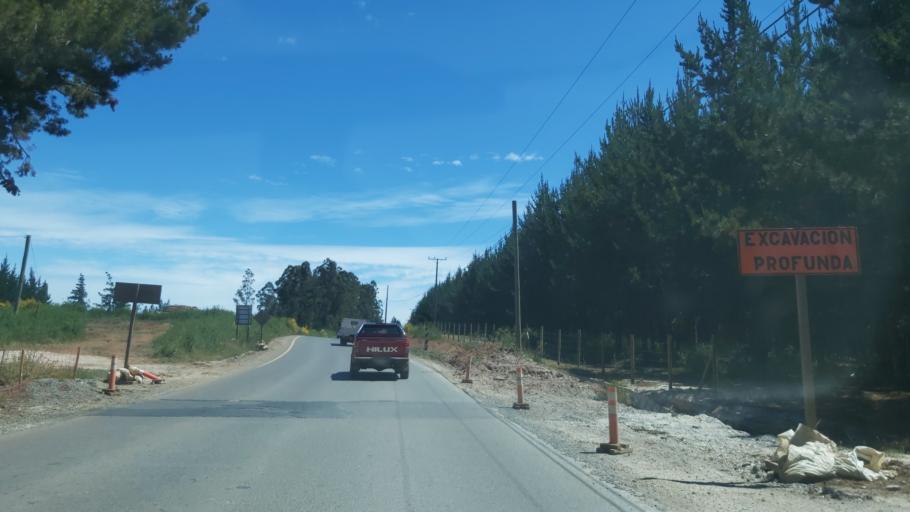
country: CL
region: Maule
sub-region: Provincia de Talca
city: Constitucion
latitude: -35.3945
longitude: -72.4287
